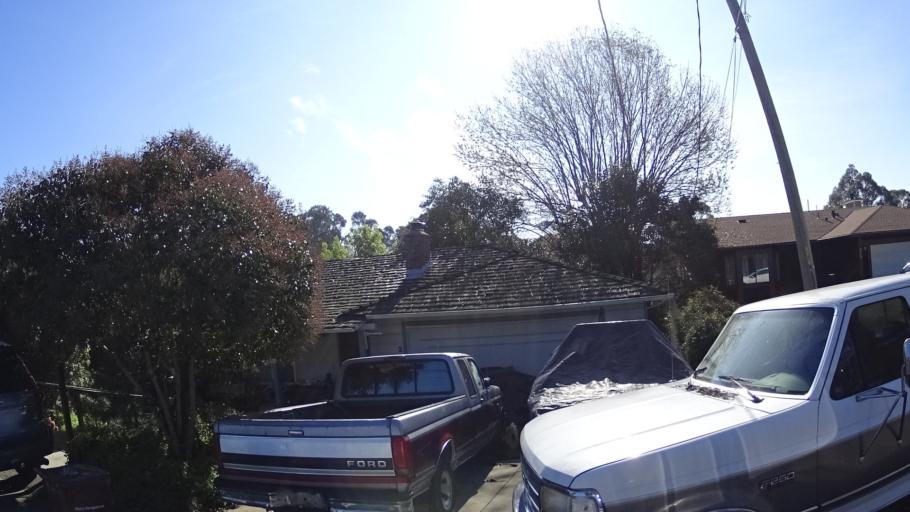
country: US
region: California
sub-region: Alameda County
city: Fairview
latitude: 37.6756
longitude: -122.0567
